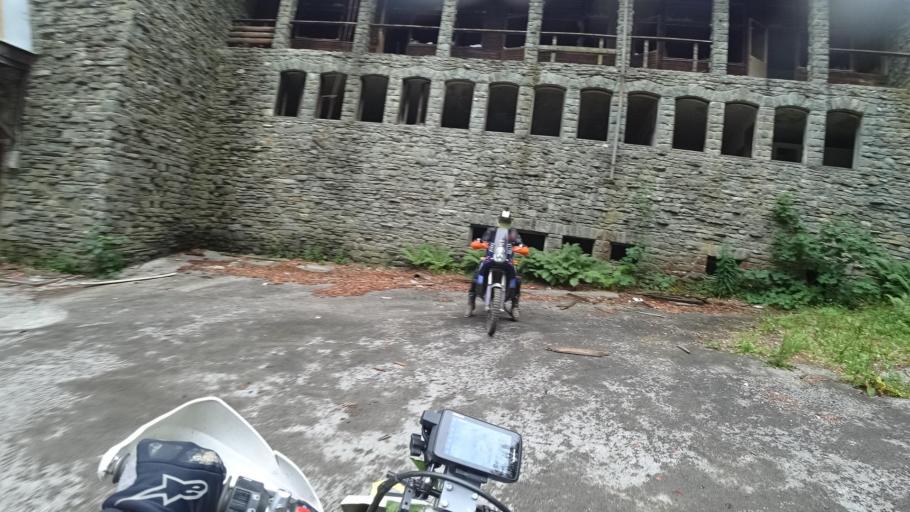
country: HR
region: Licko-Senjska
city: Jezerce
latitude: 44.9029
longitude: 15.5716
